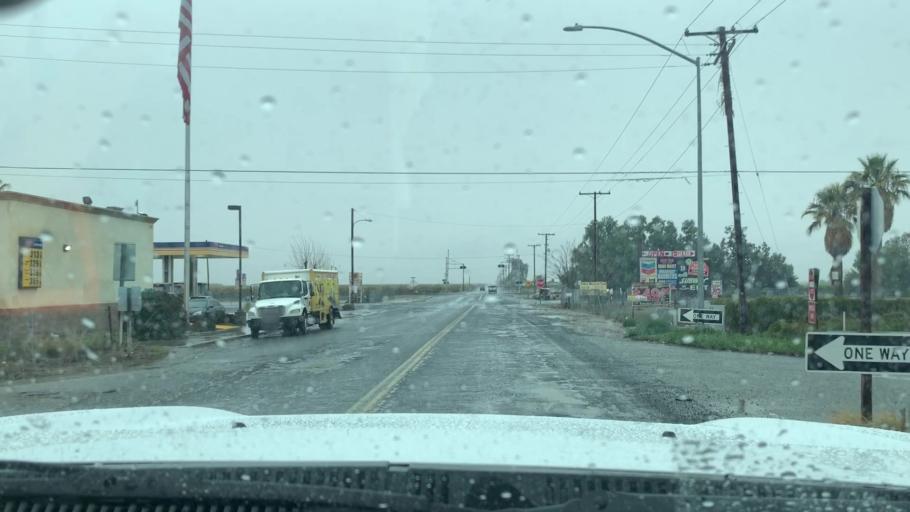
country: US
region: California
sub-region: Tulare County
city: Earlimart
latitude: 35.8919
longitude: -119.2746
